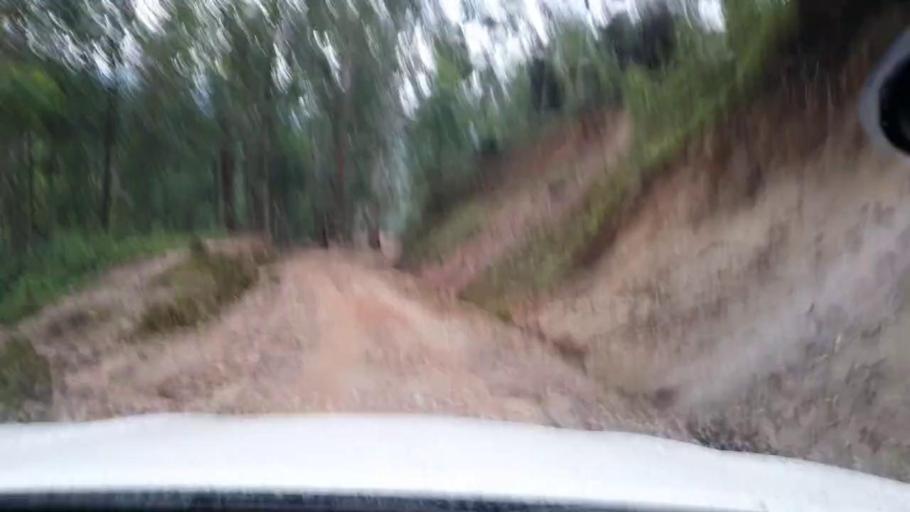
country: RW
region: Western Province
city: Cyangugu
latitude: -2.4110
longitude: 29.1985
